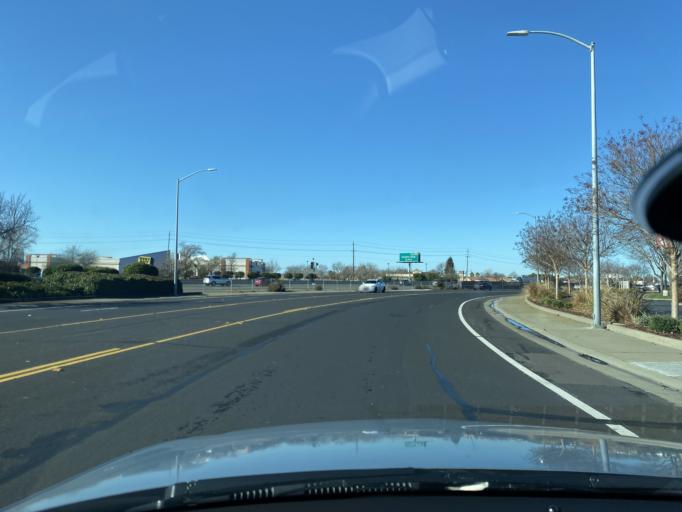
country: US
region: California
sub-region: Sacramento County
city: Elk Grove
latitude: 38.4256
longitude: -121.3952
